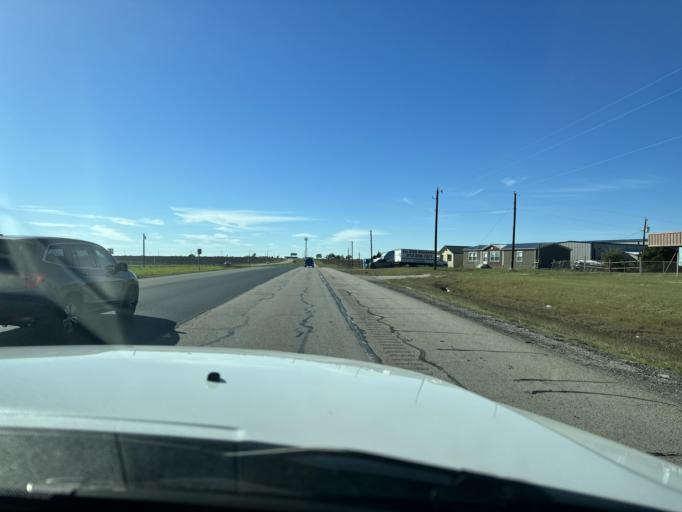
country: US
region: Texas
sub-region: Johnson County
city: Venus
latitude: 32.4350
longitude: -97.1201
